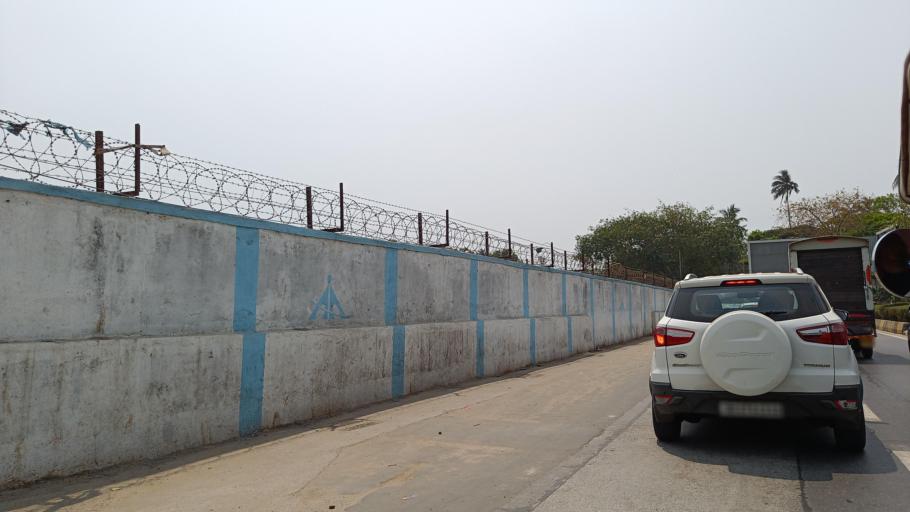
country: IN
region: Maharashtra
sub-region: Mumbai Suburban
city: Mumbai
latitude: 19.0971
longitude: 72.8270
